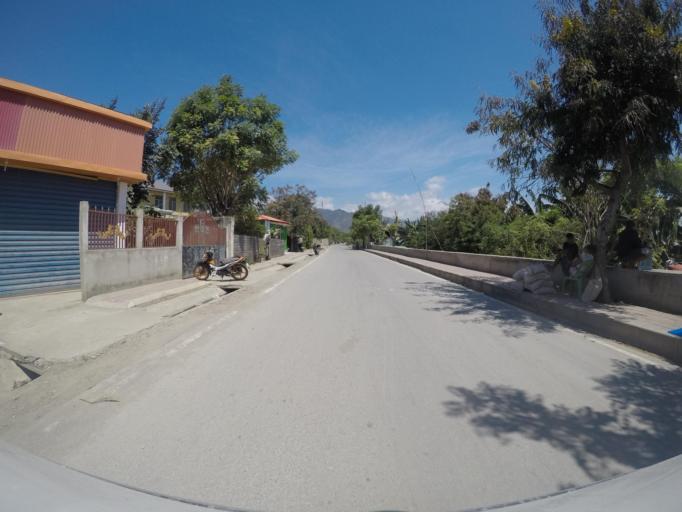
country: TL
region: Dili
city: Dili
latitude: -8.5459
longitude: 125.5362
